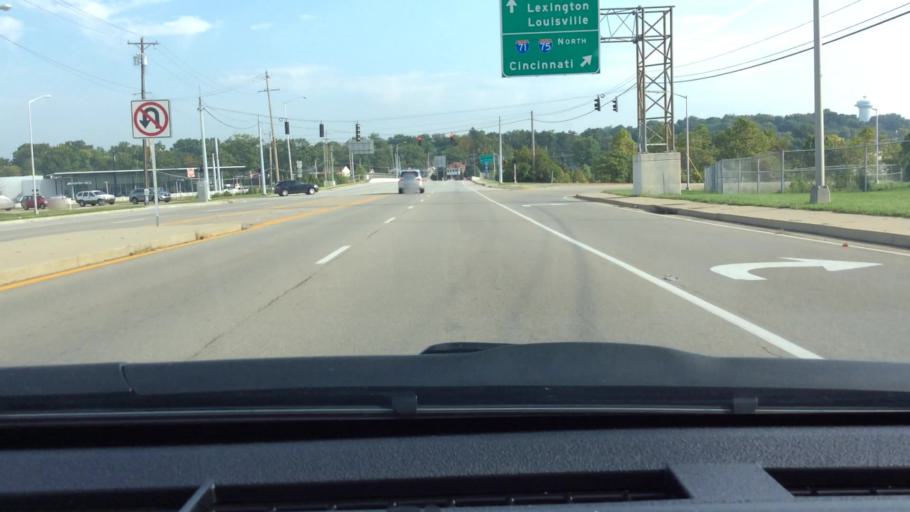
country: US
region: Kentucky
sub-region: Kenton County
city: Fort Mitchell
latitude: 39.0490
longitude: -84.5516
